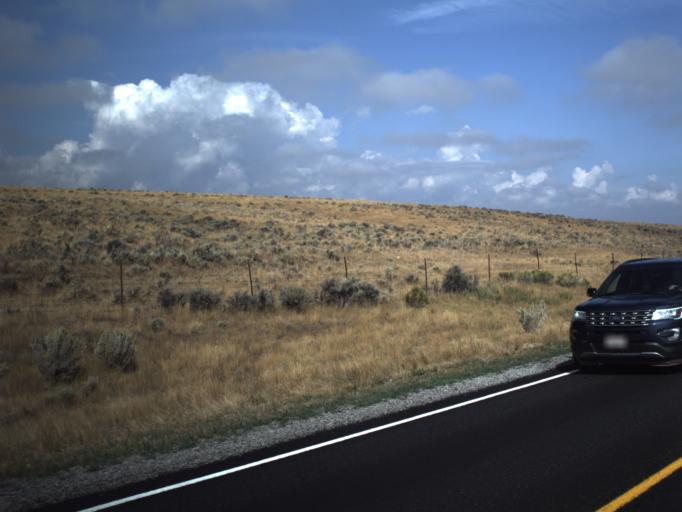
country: US
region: Utah
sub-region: Rich County
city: Randolph
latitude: 41.5526
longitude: -111.1549
